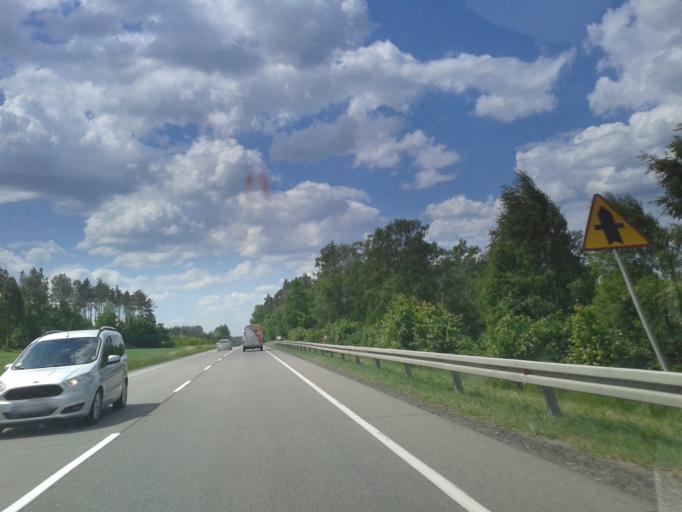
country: PL
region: Pomeranian Voivodeship
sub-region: Powiat chojnicki
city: Chojnice
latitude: 53.7123
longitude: 17.6566
